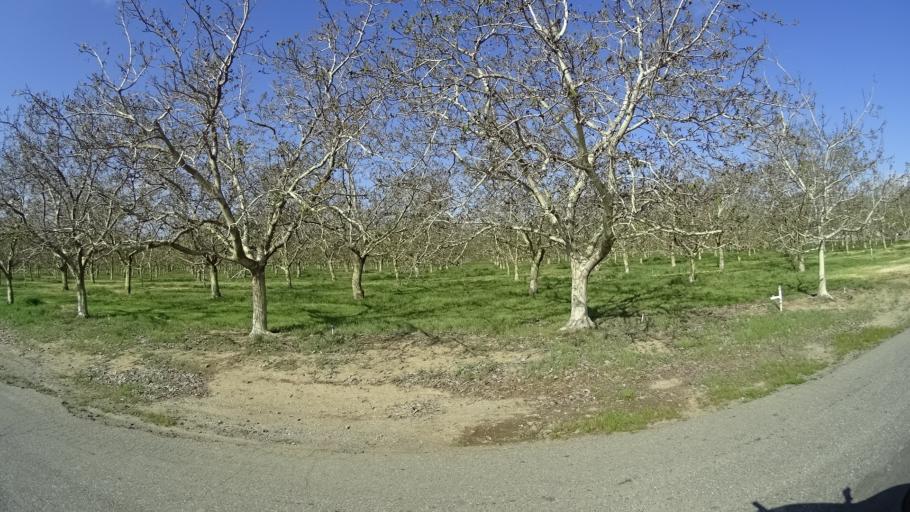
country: US
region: California
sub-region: Butte County
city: Durham
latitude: 39.5107
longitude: -121.9679
